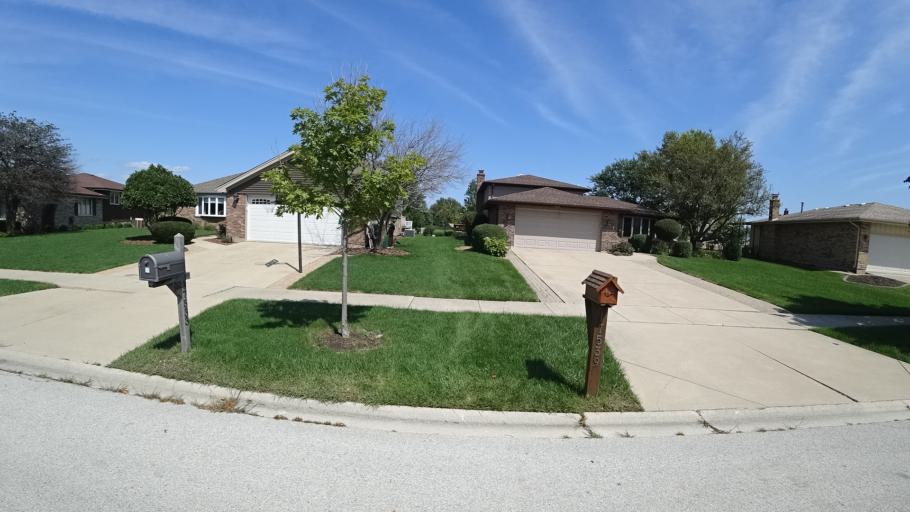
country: US
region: Illinois
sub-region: Cook County
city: Orland Hills
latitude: 41.5711
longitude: -87.8353
